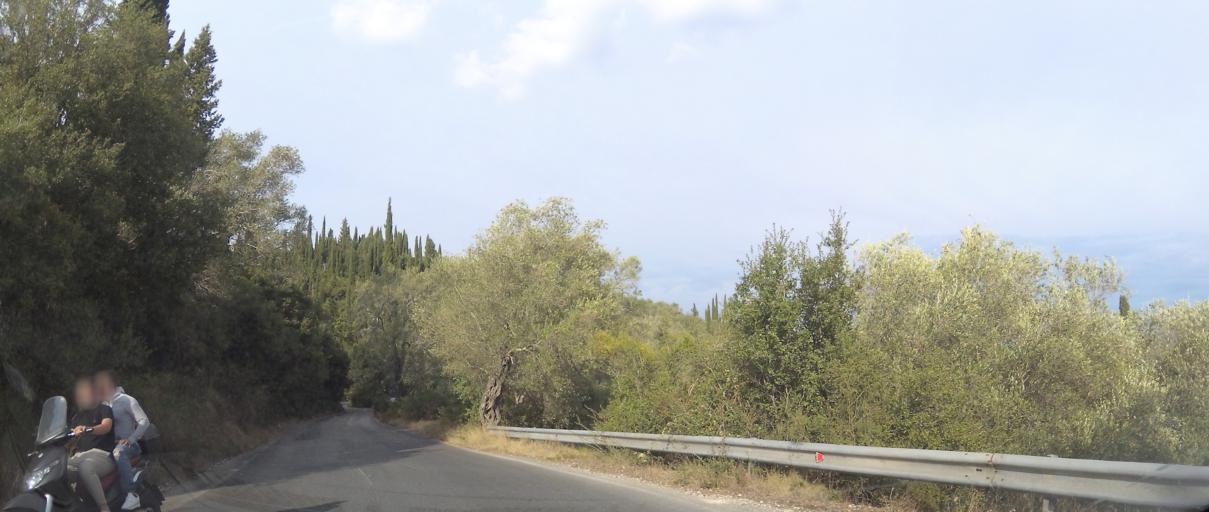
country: GR
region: Ionian Islands
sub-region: Nomos Kerkyras
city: Kynopiastes
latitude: 39.5634
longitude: 19.8715
